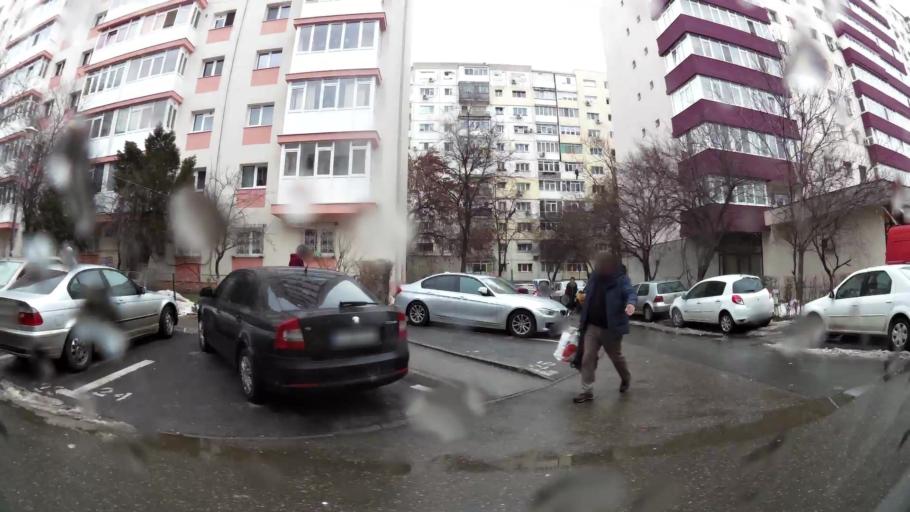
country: RO
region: Ilfov
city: Dobroesti
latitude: 44.4172
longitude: 26.1818
